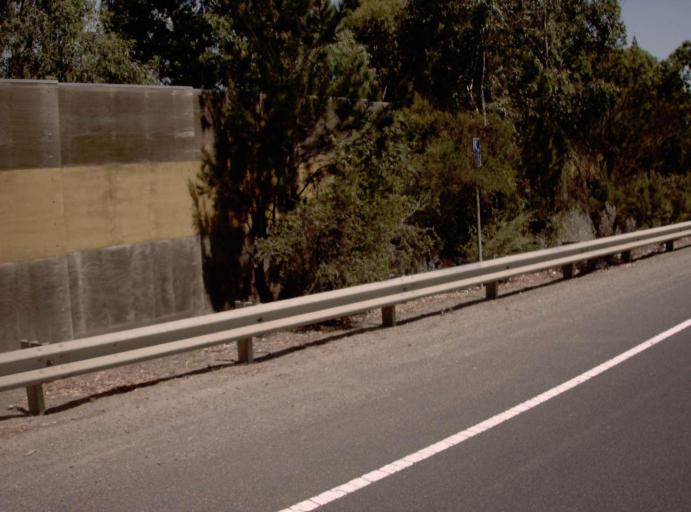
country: AU
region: Victoria
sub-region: Casey
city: Narre Warren
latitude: -38.0141
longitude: 145.3044
